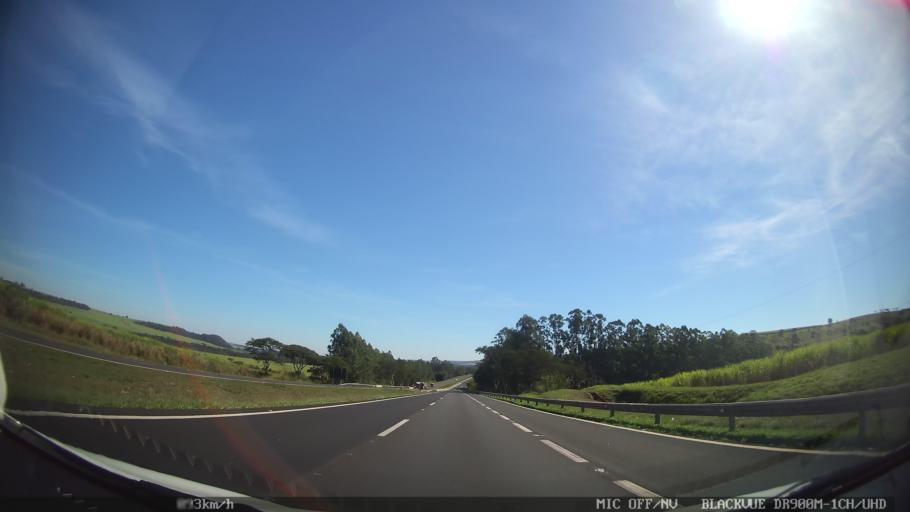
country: BR
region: Sao Paulo
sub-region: Santa Rita Do Passa Quatro
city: Santa Rita do Passa Quatro
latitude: -21.7541
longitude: -47.5661
